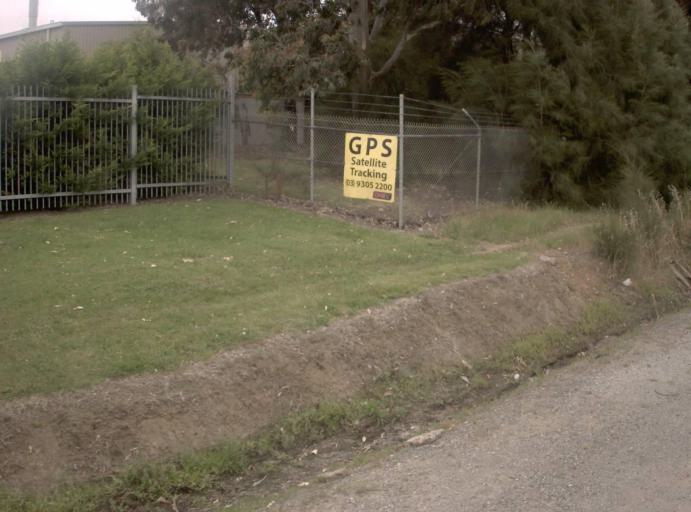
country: AU
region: Victoria
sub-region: Casey
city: Hallam
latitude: -38.0115
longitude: 145.2722
